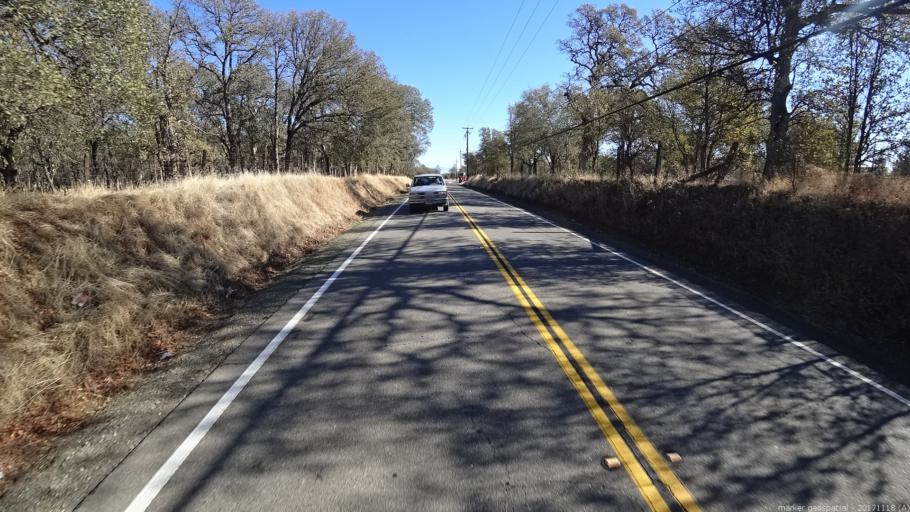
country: US
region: California
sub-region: Shasta County
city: Cottonwood
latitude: 40.3887
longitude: -122.3799
